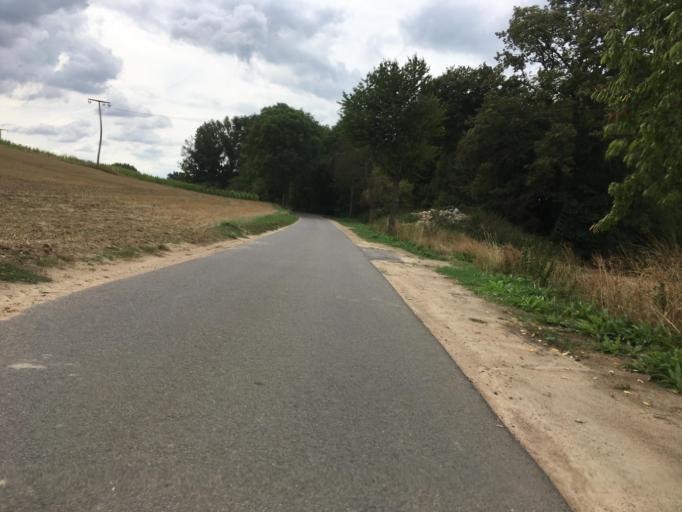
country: DE
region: Brandenburg
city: Prenzlau
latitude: 53.2593
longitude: 13.8862
